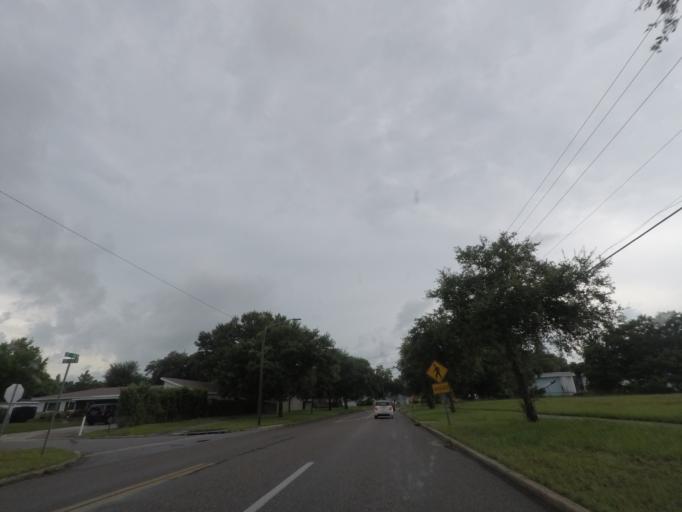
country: US
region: Florida
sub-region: Pinellas County
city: Kenneth City
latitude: 27.7919
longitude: -82.7431
